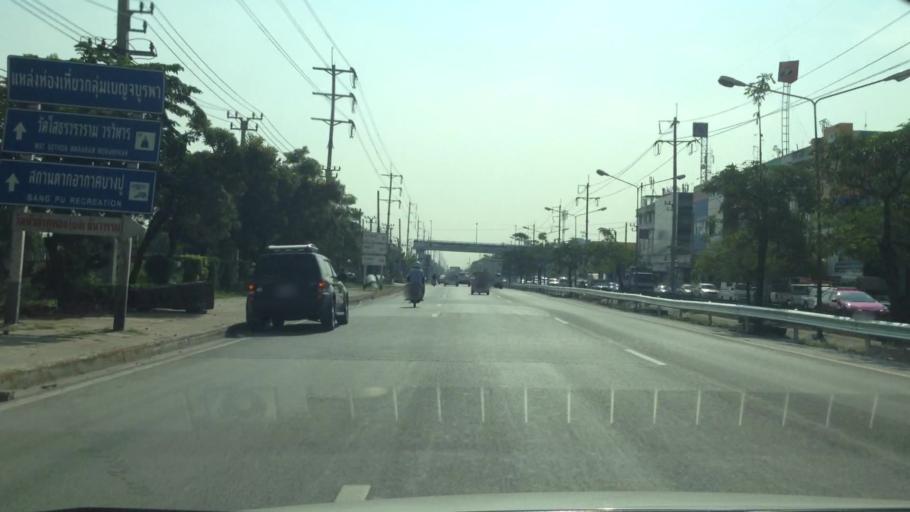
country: TH
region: Samut Prakan
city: Samut Prakan
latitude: 13.5358
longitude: 100.6261
